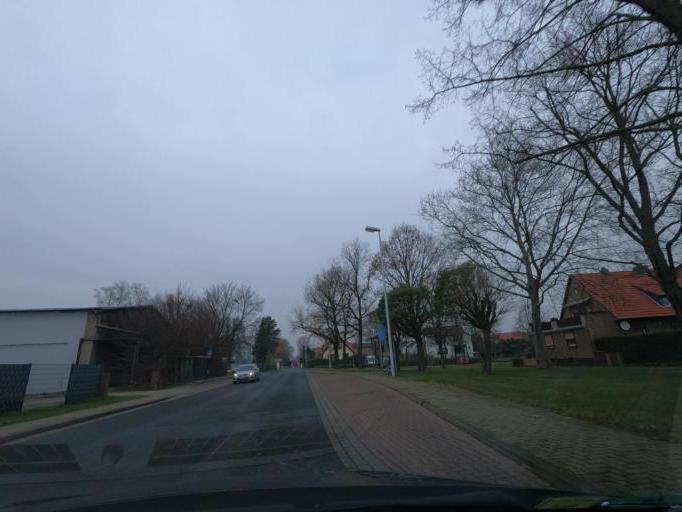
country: DE
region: Lower Saxony
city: Wolfenbuettel
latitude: 52.1924
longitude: 10.5887
